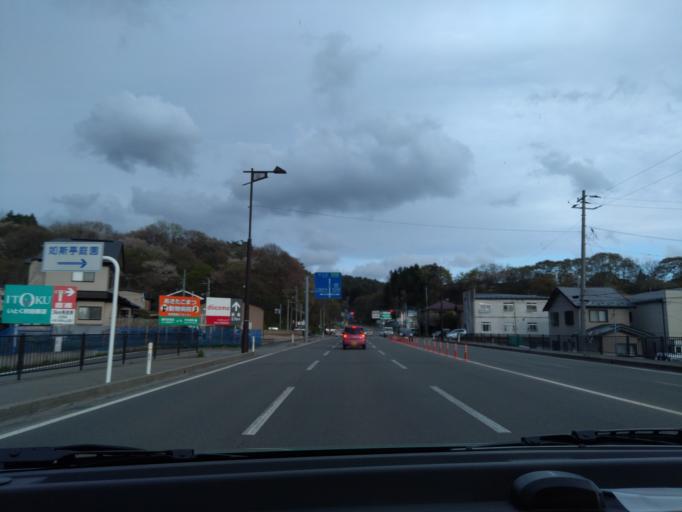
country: JP
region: Akita
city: Akita
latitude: 39.7469
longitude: 140.1304
